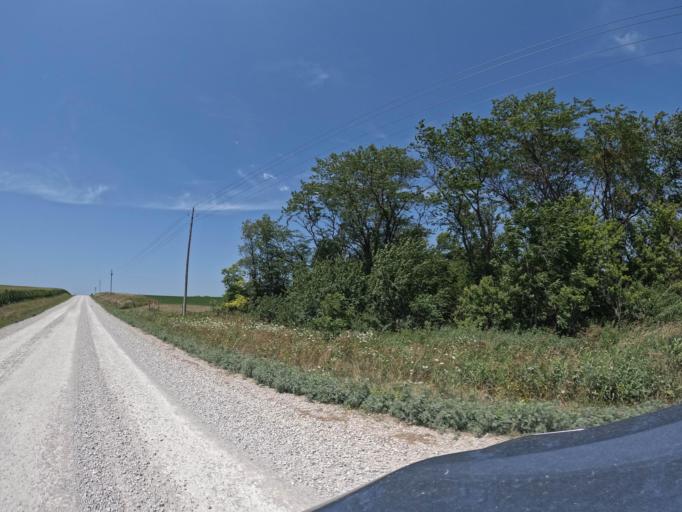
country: US
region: Iowa
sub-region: Henry County
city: Mount Pleasant
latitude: 40.9269
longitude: -91.6410
